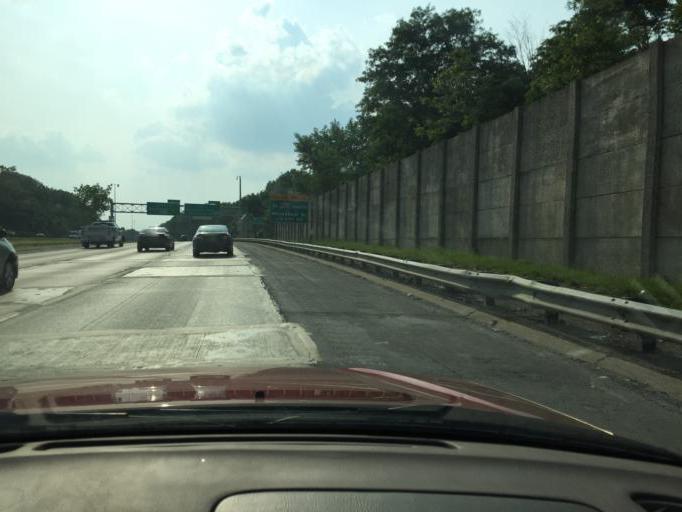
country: US
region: New York
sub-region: Westchester County
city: Pelham Manor
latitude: 40.8866
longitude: -73.8098
